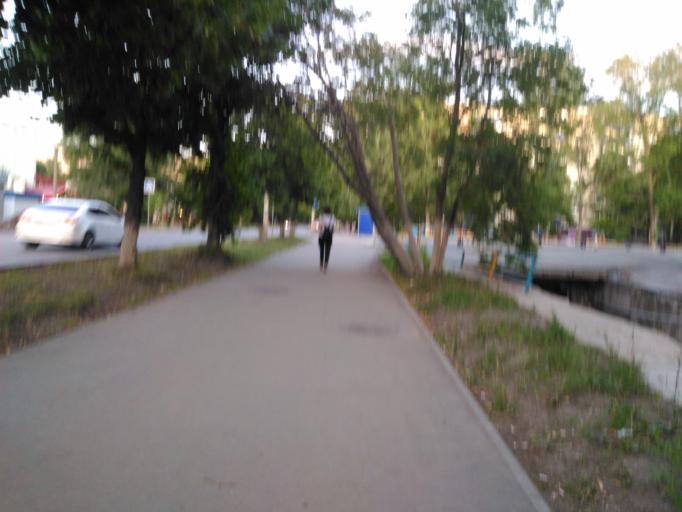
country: RU
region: Ulyanovsk
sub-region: Ulyanovskiy Rayon
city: Ulyanovsk
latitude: 54.2835
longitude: 48.2889
